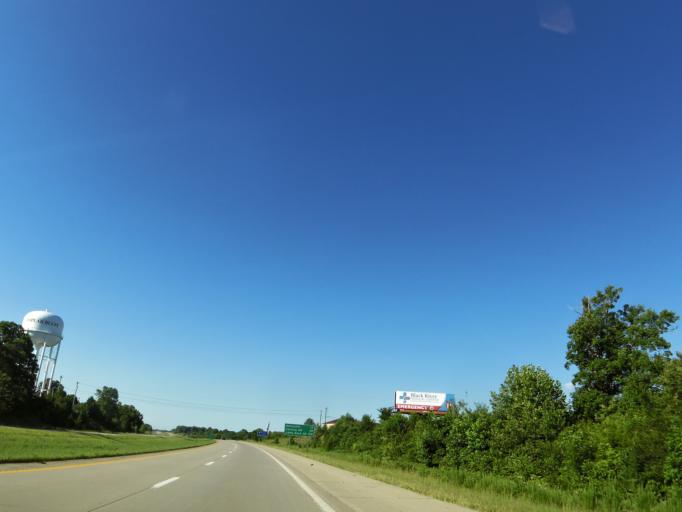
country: US
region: Missouri
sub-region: Butler County
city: Poplar Bluff
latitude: 36.7762
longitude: -90.4554
